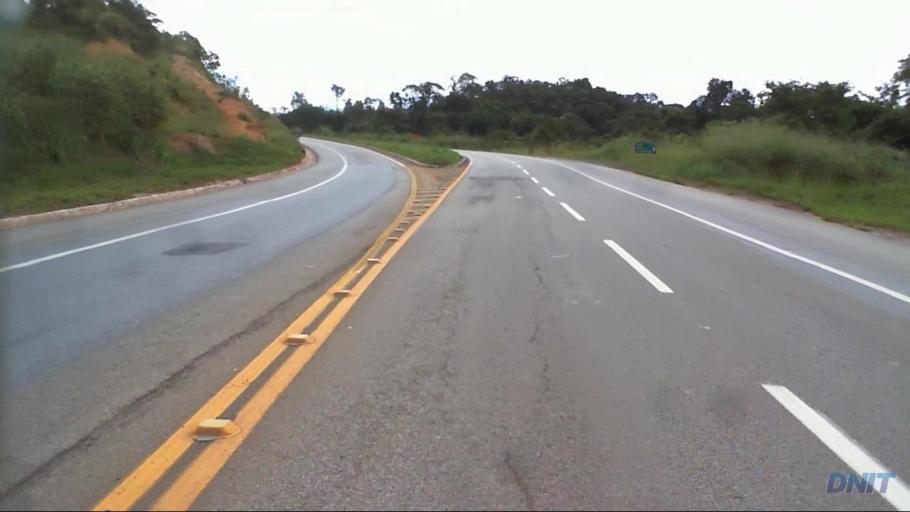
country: BR
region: Minas Gerais
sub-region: Caete
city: Caete
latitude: -19.7937
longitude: -43.6798
